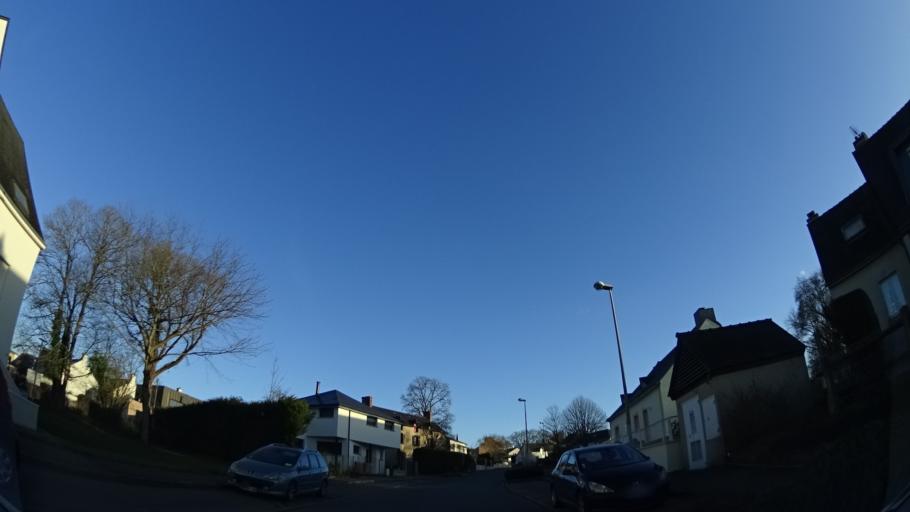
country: FR
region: Brittany
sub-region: Departement d'Ille-et-Vilaine
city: Betton
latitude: 48.1811
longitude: -1.6516
